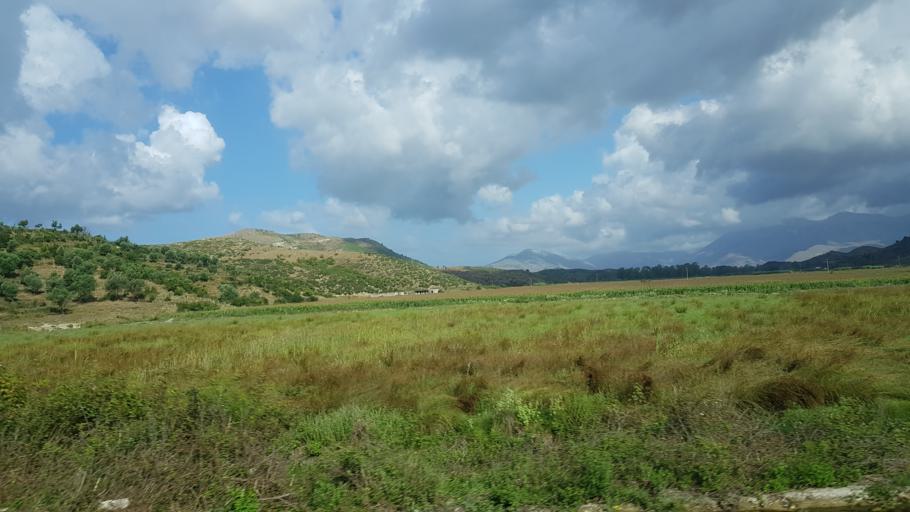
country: AL
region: Vlore
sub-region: Rrethi i Delvines
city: Mesopotam
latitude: 39.9057
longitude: 20.0855
